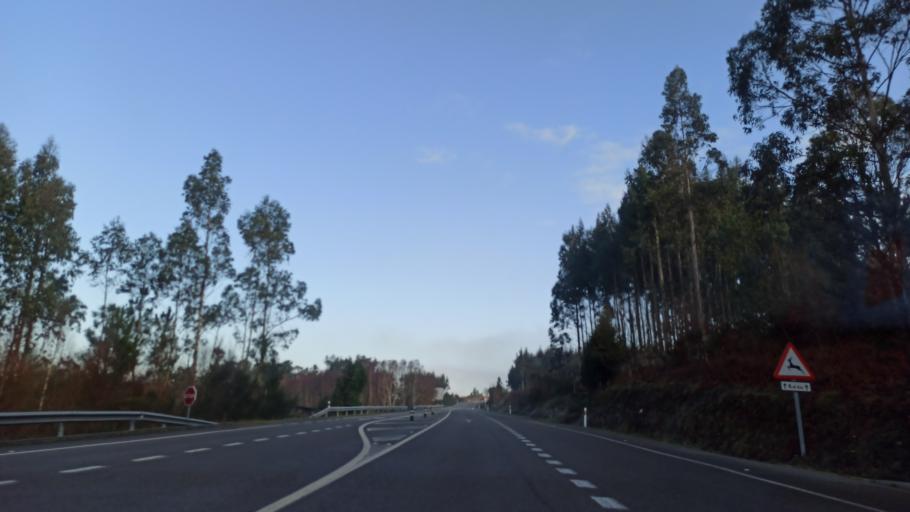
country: ES
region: Galicia
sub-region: Provincia da Coruna
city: As Pontes de Garcia Rodriguez
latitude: 43.4707
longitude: -7.8547
